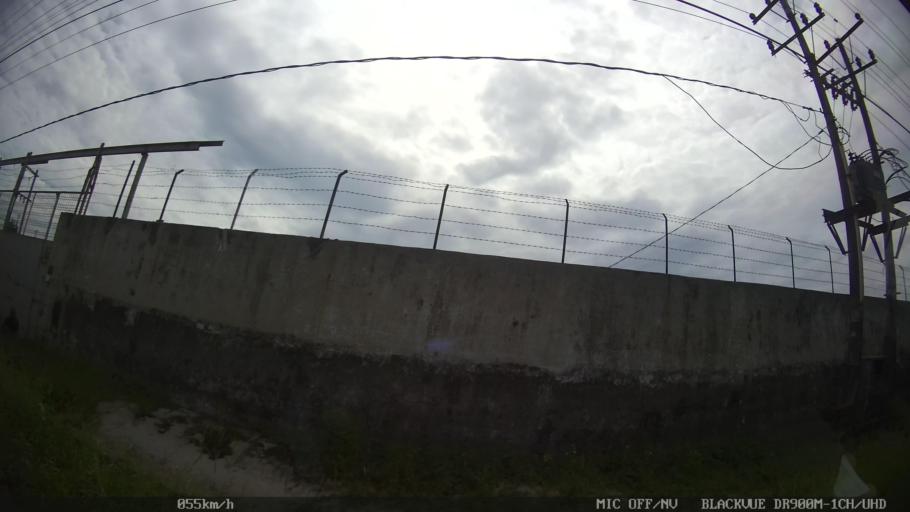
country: ID
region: North Sumatra
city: Sunggal
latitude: 3.5960
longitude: 98.5832
